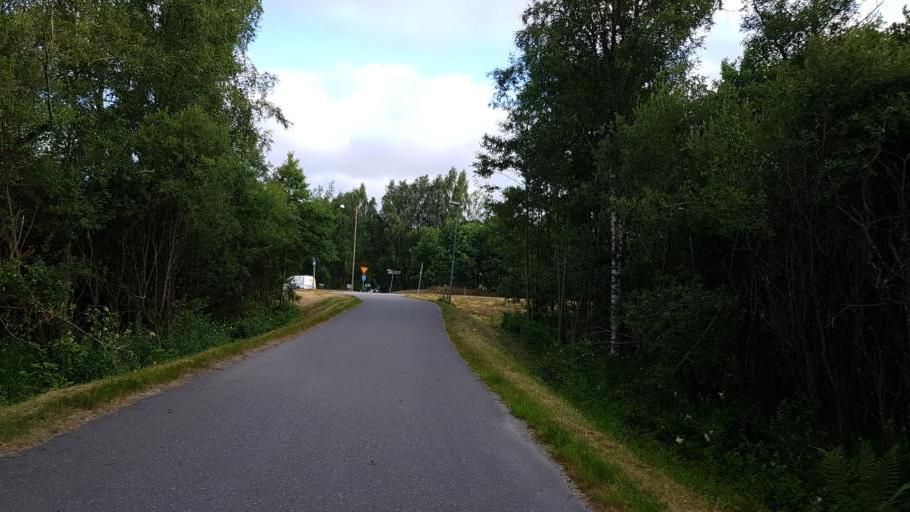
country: SE
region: Vaestra Goetaland
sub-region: Harryda Kommun
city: Molnlycke
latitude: 57.6567
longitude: 12.1092
